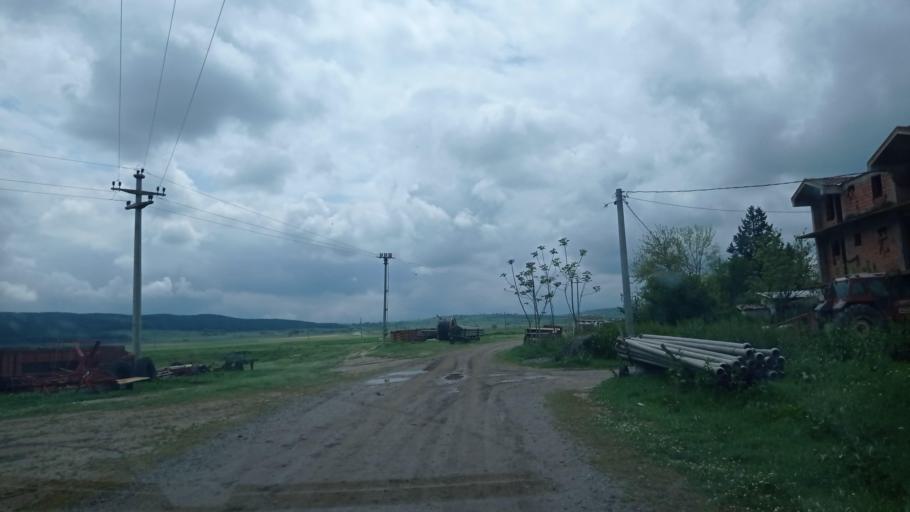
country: MK
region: Lozovo
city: Lozovo
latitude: 41.7631
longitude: 21.8923
